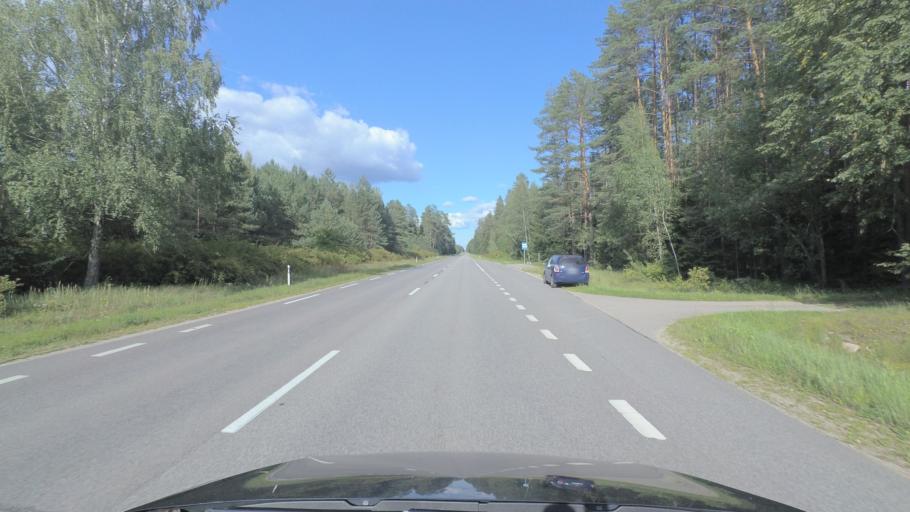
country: LT
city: Pabrade
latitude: 54.9570
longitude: 25.6831
